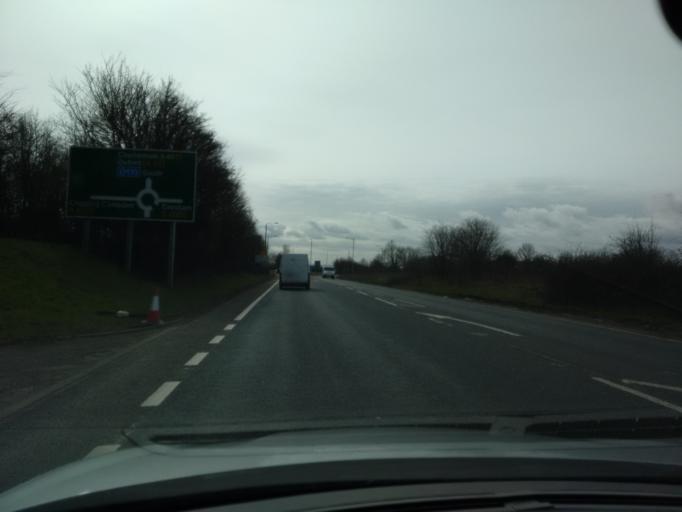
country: GB
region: England
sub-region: Worcestershire
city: Badsey
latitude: 52.0940
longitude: -1.9218
